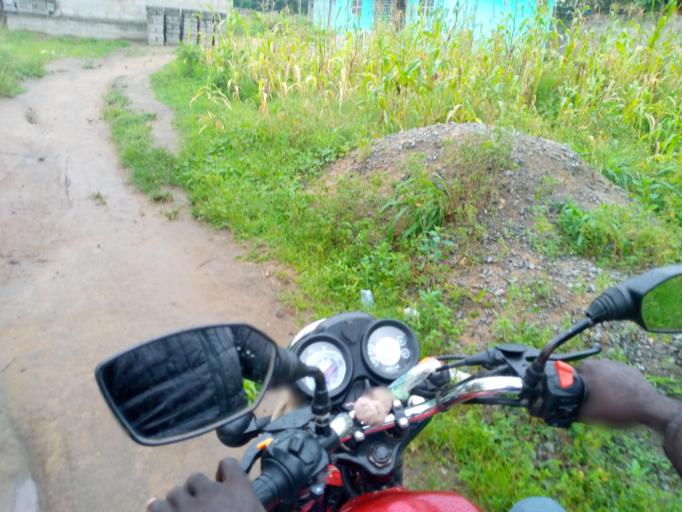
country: SL
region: Eastern Province
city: Kenema
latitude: 7.8458
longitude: -11.2058
